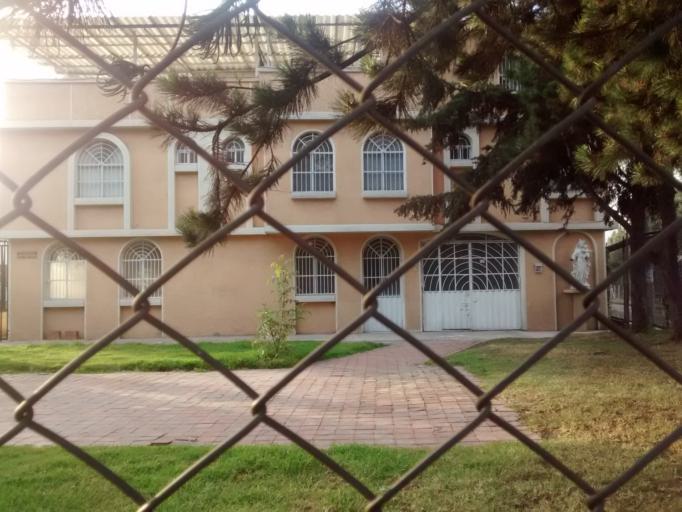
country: CO
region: Bogota D.C.
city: Bogota
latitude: 4.6233
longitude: -74.1230
